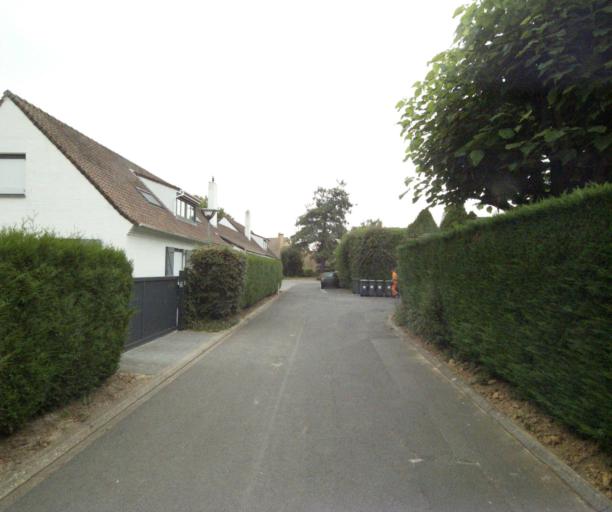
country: FR
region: Nord-Pas-de-Calais
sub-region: Departement du Nord
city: Bondues
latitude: 50.7004
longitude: 3.0887
